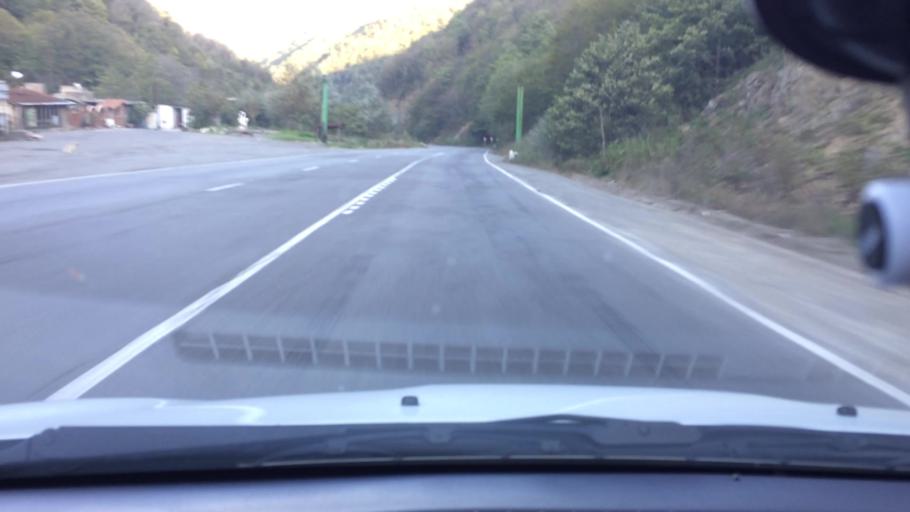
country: GE
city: Surami
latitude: 42.0870
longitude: 43.4667
